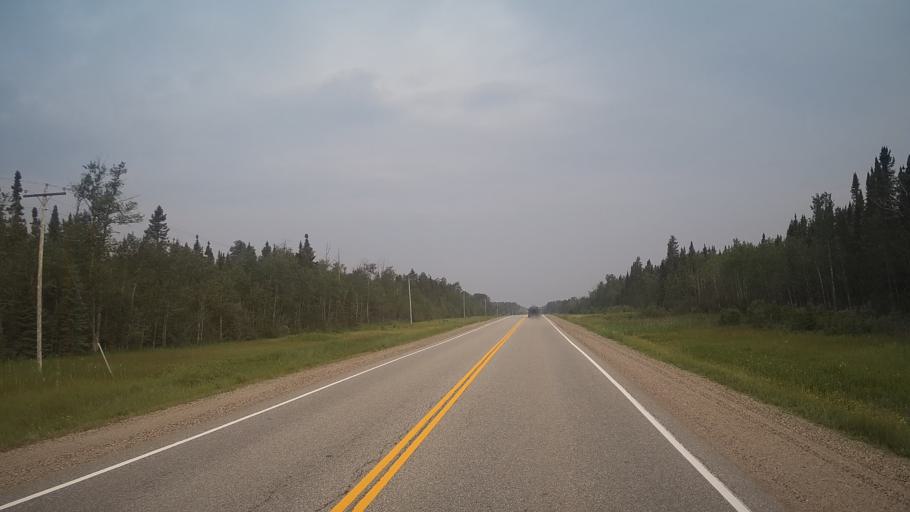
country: CA
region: Ontario
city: Hearst
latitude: 49.7268
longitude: -83.8896
